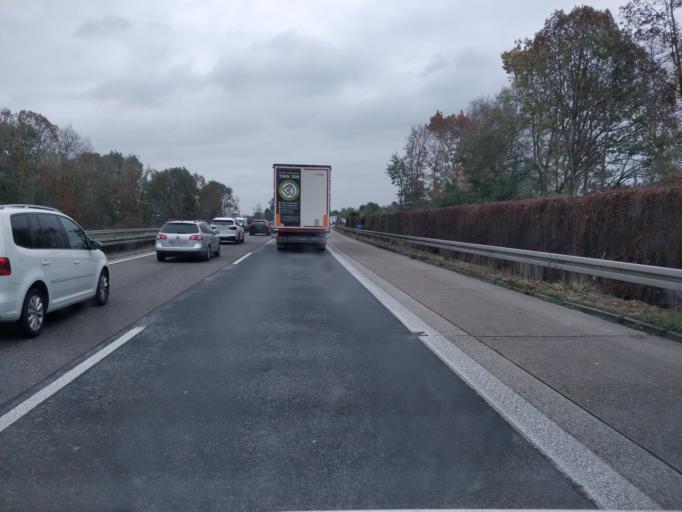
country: DE
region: North Rhine-Westphalia
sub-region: Regierungsbezirk Dusseldorf
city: Hamminkeln
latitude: 51.7437
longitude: 6.6038
